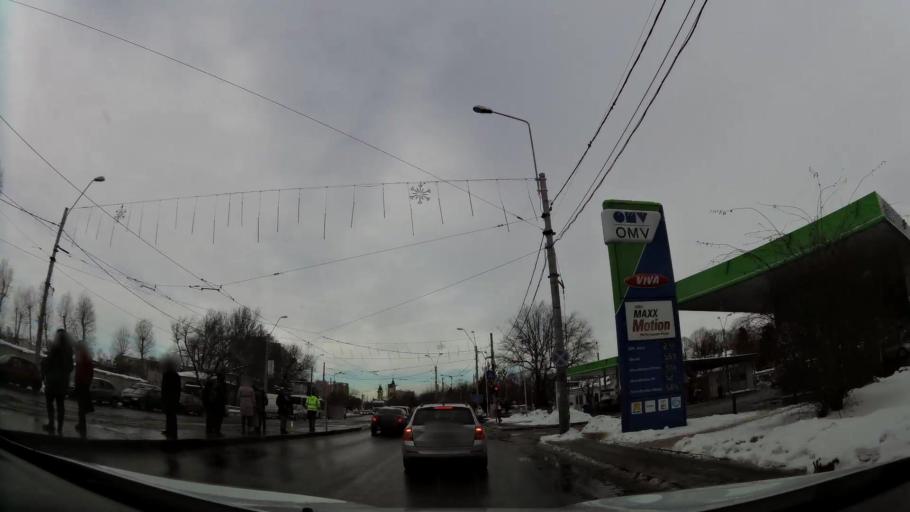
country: RO
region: Bucuresti
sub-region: Municipiul Bucuresti
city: Bucuresti
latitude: 44.4023
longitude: 26.0975
